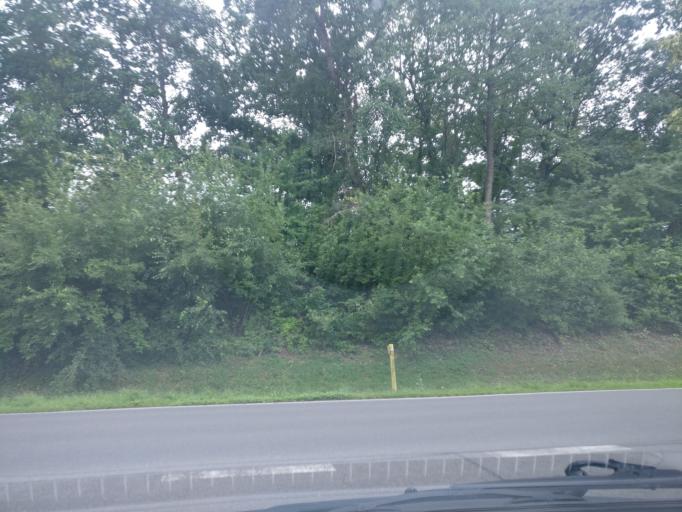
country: DE
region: Hesse
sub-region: Regierungsbezirk Kassel
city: Baunatal
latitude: 51.2784
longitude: 9.3635
